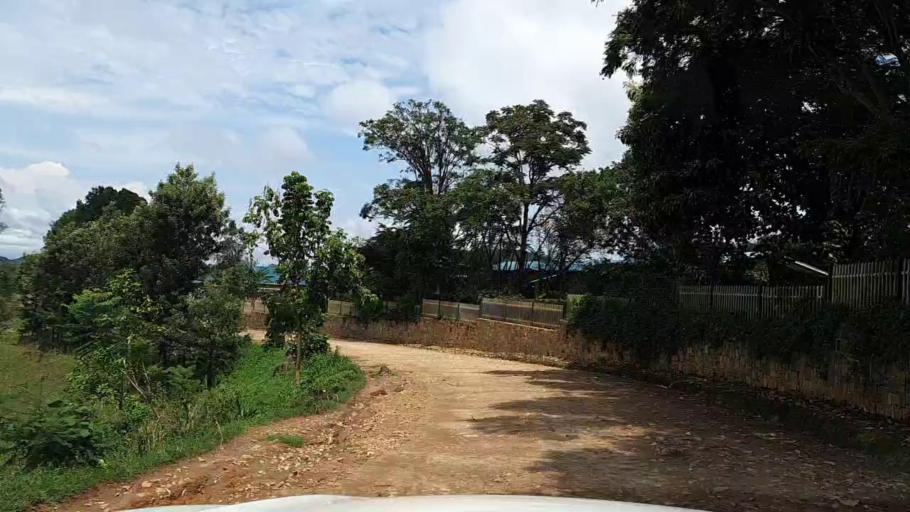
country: RW
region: Southern Province
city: Gikongoro
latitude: -2.3349
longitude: 29.5226
